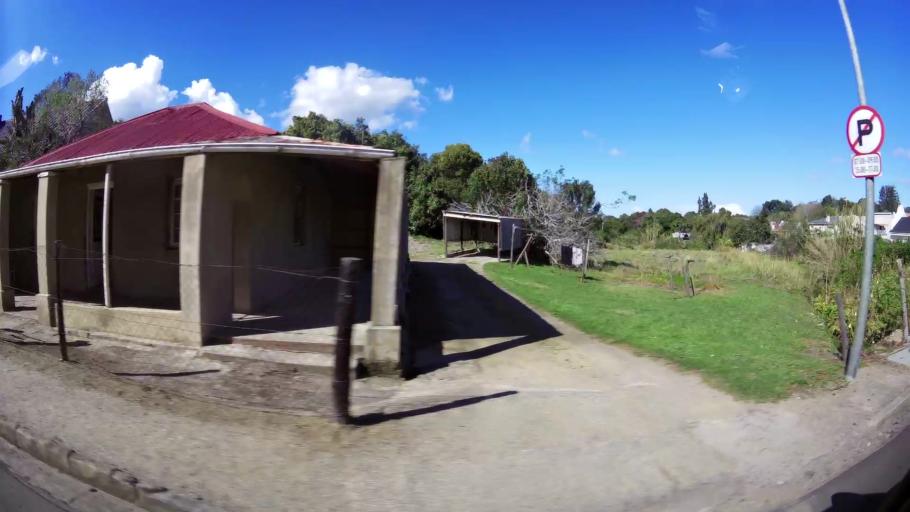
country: ZA
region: Western Cape
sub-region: Eden District Municipality
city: George
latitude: -33.9506
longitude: 22.4710
